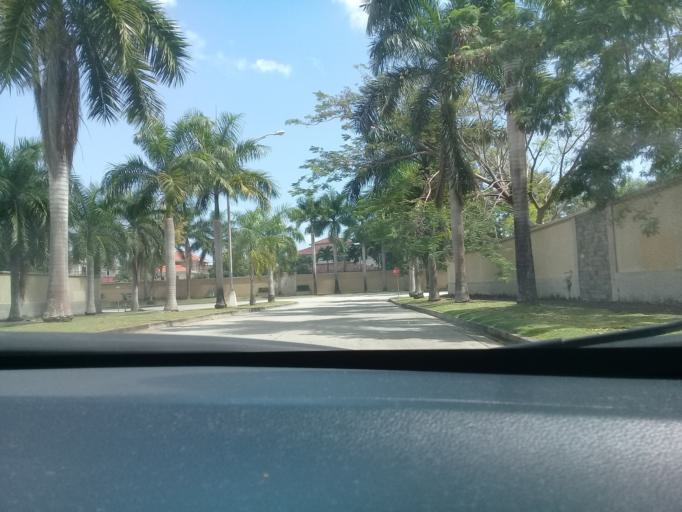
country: PA
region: Panama
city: San Miguelito
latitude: 9.0135
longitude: -79.4625
